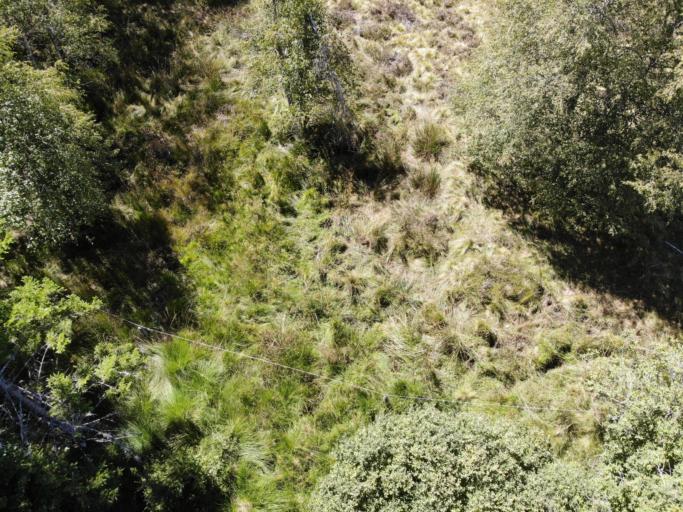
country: FR
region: Languedoc-Roussillon
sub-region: Departement de la Lozere
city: Chirac
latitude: 44.5675
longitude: 3.1607
